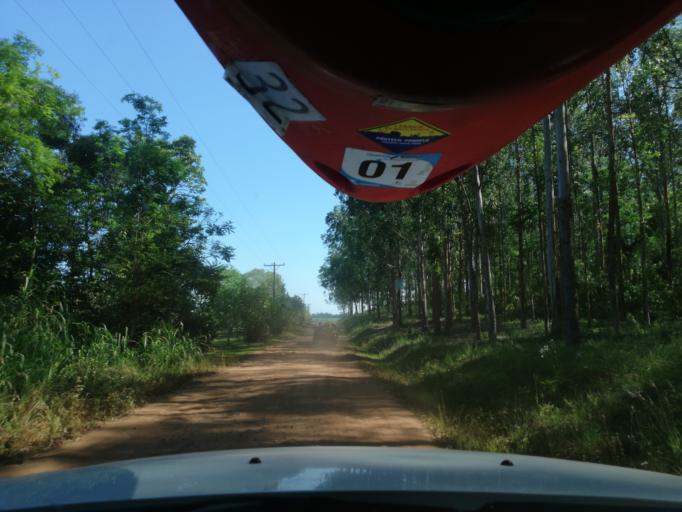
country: AR
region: Misiones
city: Puerto Leoni
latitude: -26.9635
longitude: -55.1525
